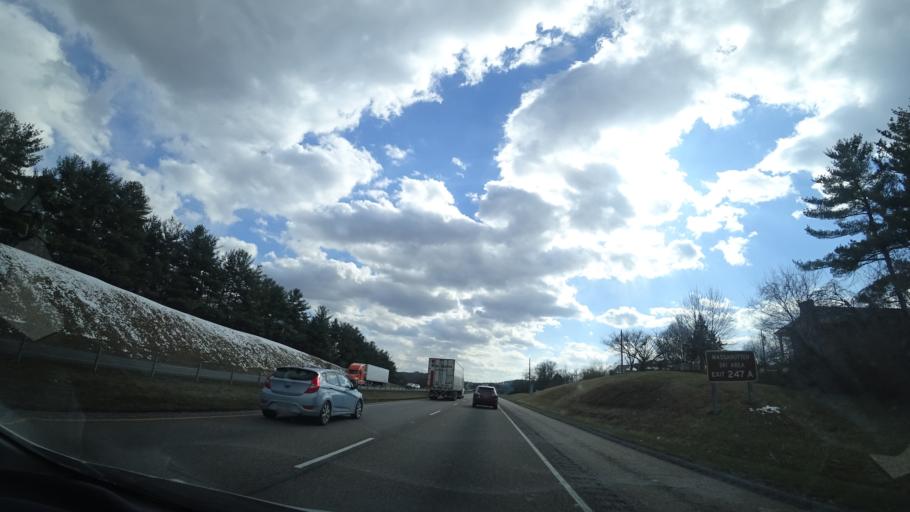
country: US
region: Virginia
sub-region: City of Harrisonburg
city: Harrisonburg
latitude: 38.4443
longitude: -78.8436
